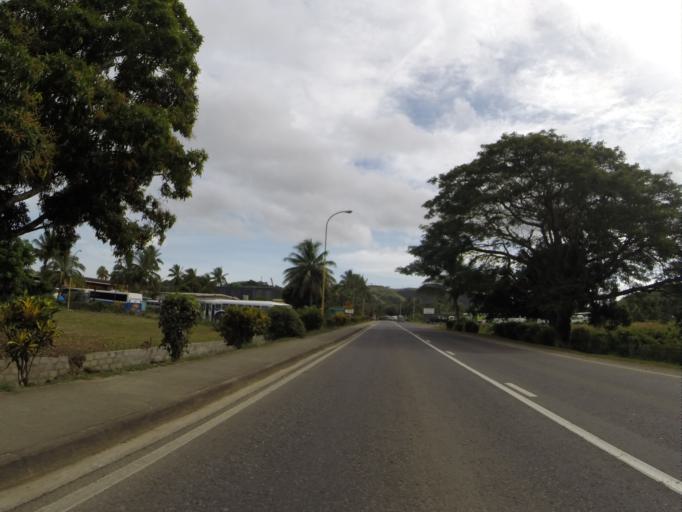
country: FJ
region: Western
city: Nadi
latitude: -18.1458
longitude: 177.5127
